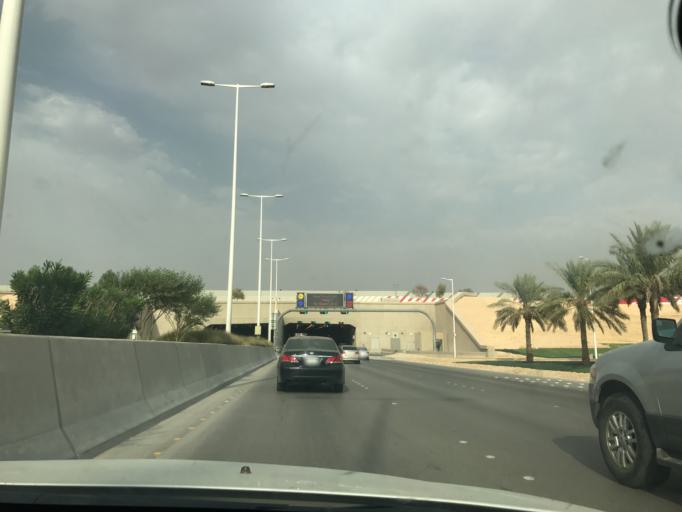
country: SA
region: Ar Riyad
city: Riyadh
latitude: 24.7273
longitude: 46.7108
